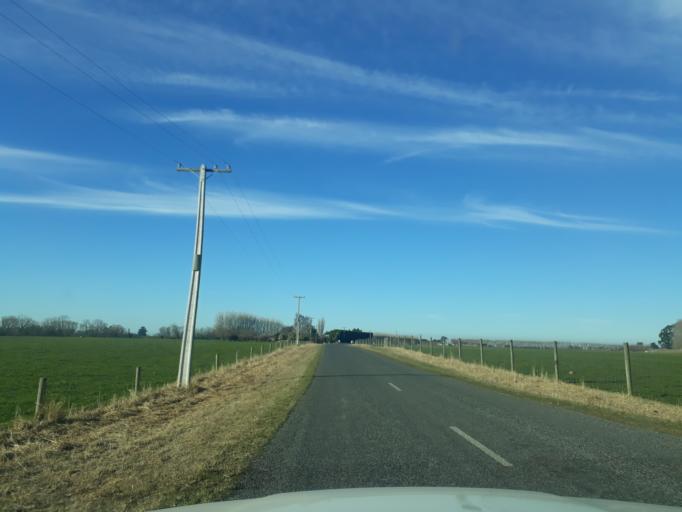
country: NZ
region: Canterbury
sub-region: Timaru District
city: Timaru
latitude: -44.2691
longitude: 171.3376
